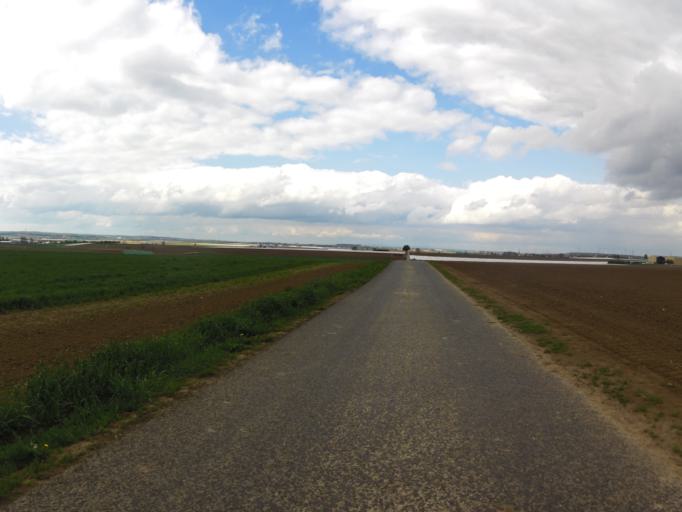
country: DE
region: Bavaria
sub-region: Regierungsbezirk Unterfranken
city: Oberpleichfeld
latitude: 49.8584
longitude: 10.0827
